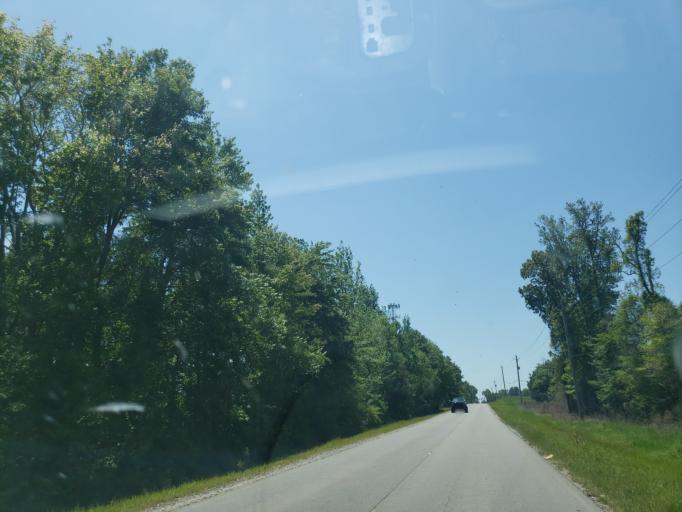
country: US
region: Alabama
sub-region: Madison County
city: Harvest
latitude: 34.8892
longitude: -86.7371
